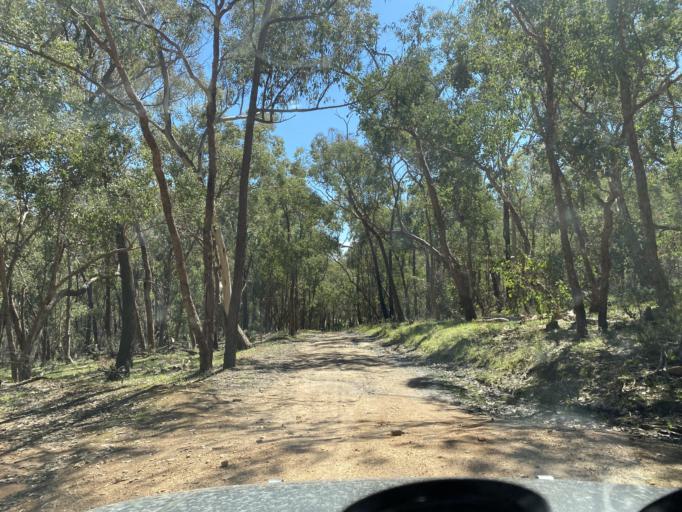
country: AU
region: Victoria
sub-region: Benalla
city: Benalla
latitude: -36.6958
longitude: 146.1481
